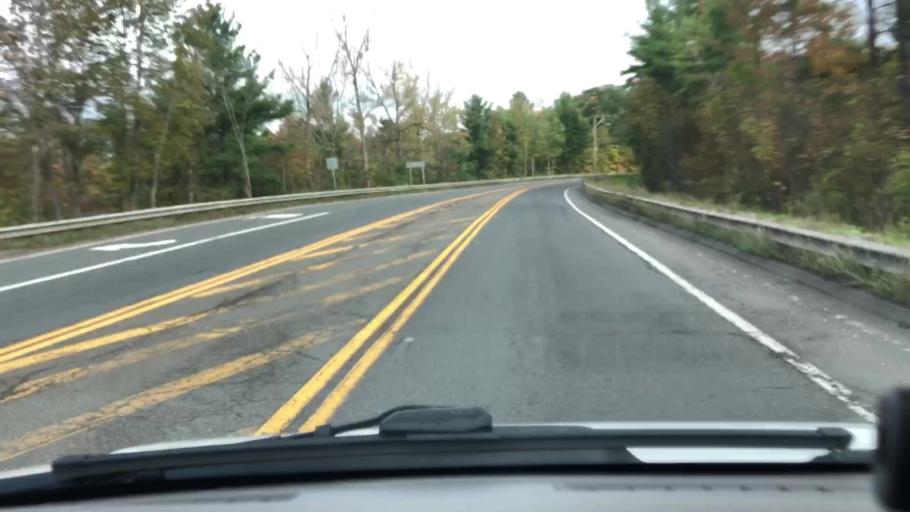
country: US
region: Massachusetts
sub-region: Berkshire County
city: Lanesborough
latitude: 42.4891
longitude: -73.2030
